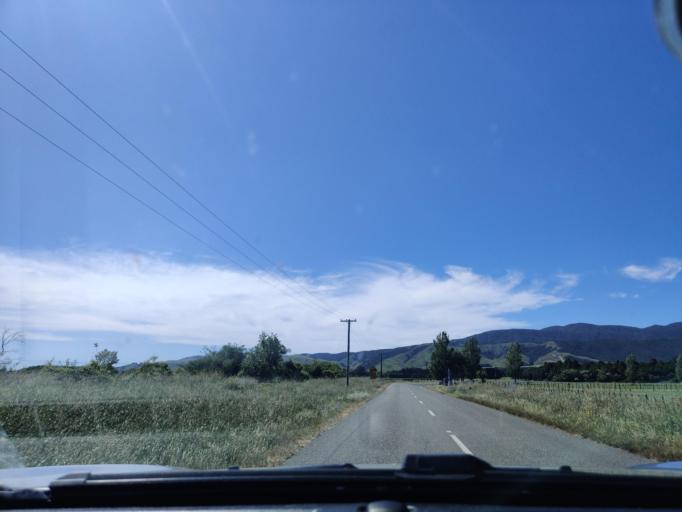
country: NZ
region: Wellington
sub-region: Upper Hutt City
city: Upper Hutt
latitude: -41.2881
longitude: 175.2694
